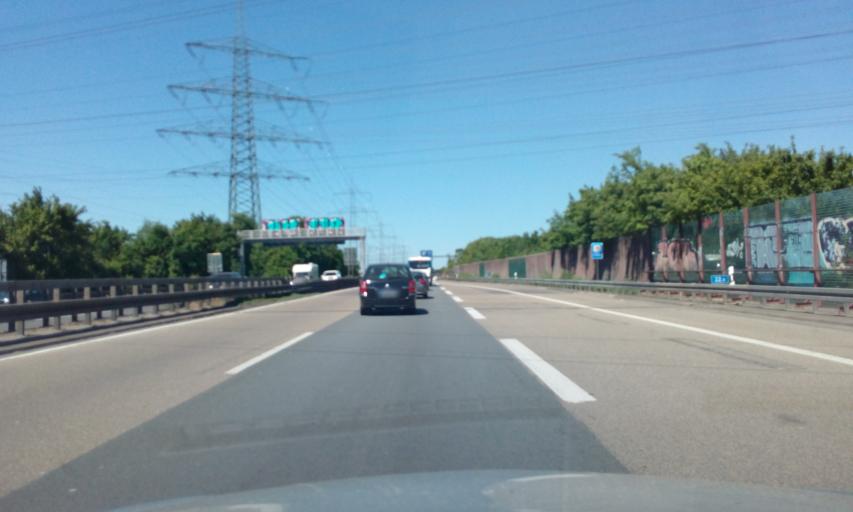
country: DE
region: North Rhine-Westphalia
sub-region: Regierungsbezirk Koln
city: Troisdorf
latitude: 50.7960
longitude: 7.1451
